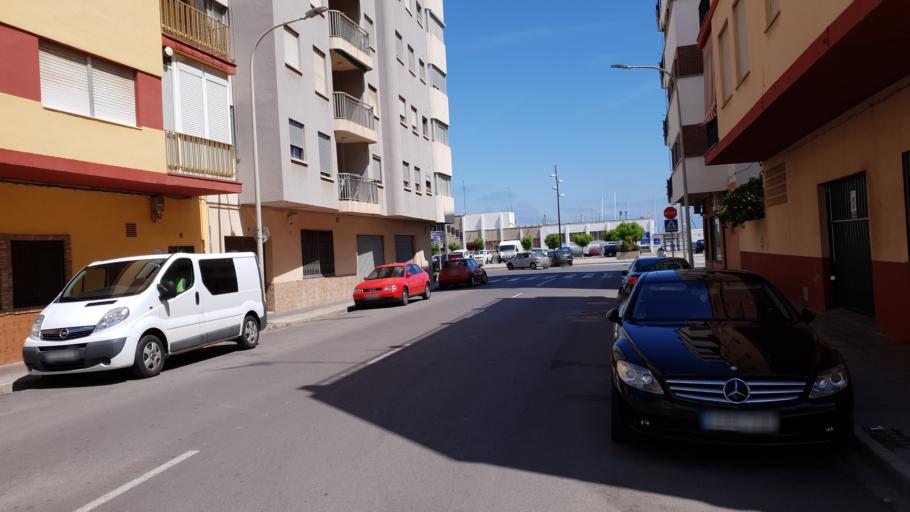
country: ES
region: Valencia
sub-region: Provincia de Castello
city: Burriana
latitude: 39.8639
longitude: -0.0755
